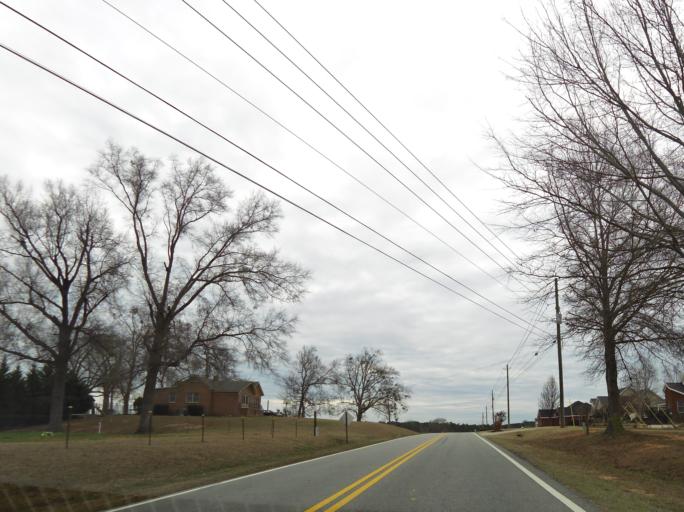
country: US
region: Georgia
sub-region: Bibb County
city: West Point
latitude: 32.8319
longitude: -83.8216
